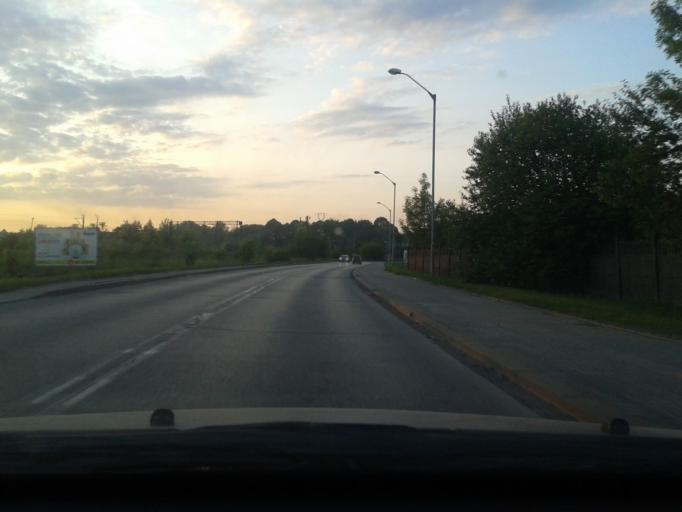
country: PL
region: Lesser Poland Voivodeship
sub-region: Powiat oswiecimski
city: Brzezinka
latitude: 50.0333
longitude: 19.1931
